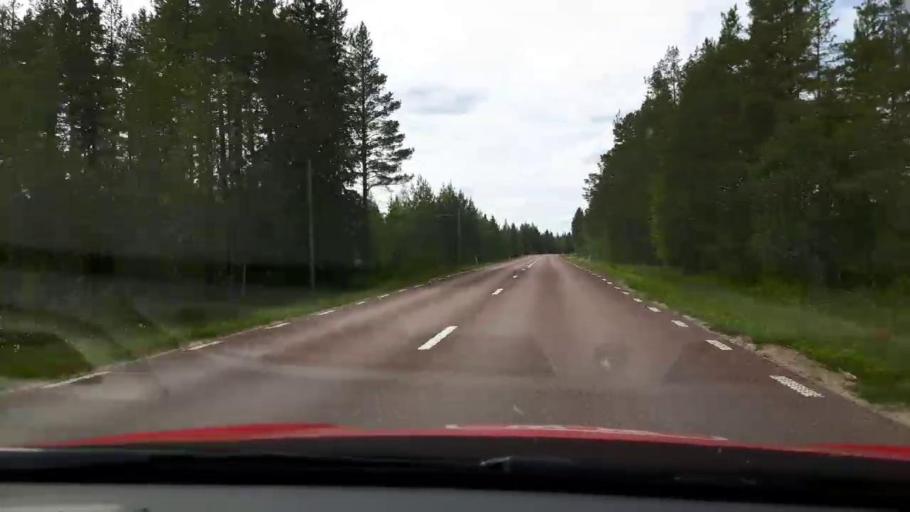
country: SE
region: Jaemtland
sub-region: Harjedalens Kommun
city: Sveg
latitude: 62.0570
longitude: 14.5656
